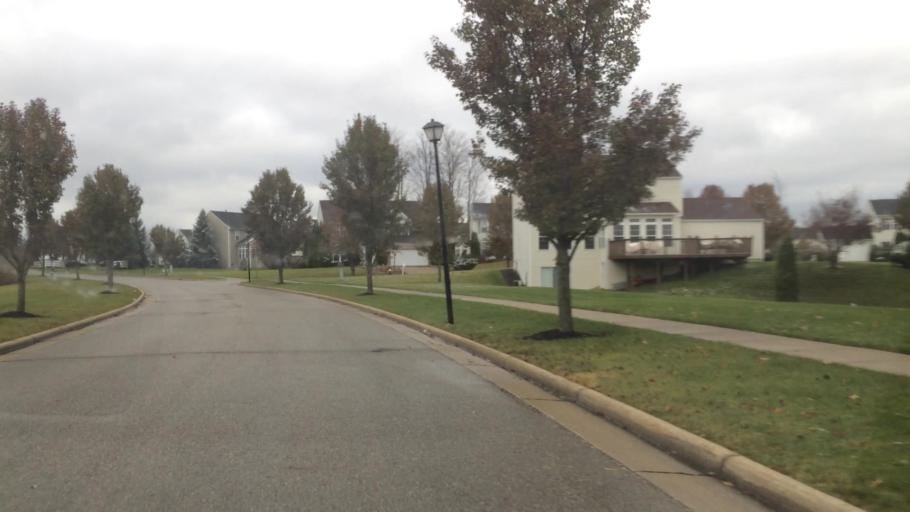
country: US
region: Ohio
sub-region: Portage County
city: Streetsboro
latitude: 41.2649
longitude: -81.3684
